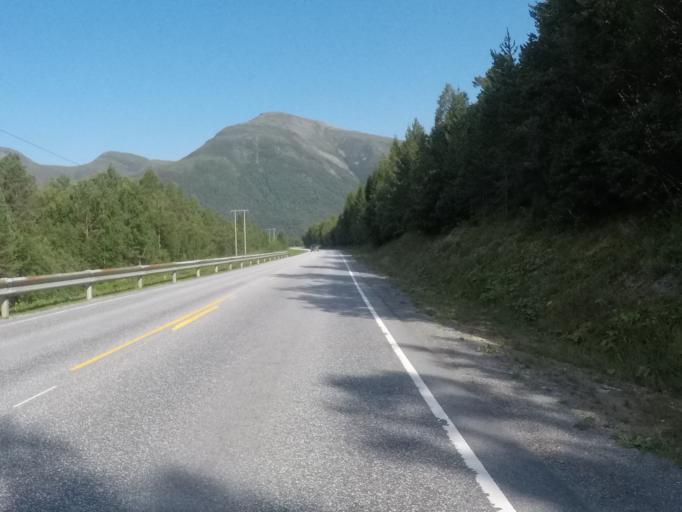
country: NO
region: More og Romsdal
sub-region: Gjemnes
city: Batnfjordsora
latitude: 62.8443
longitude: 7.5983
